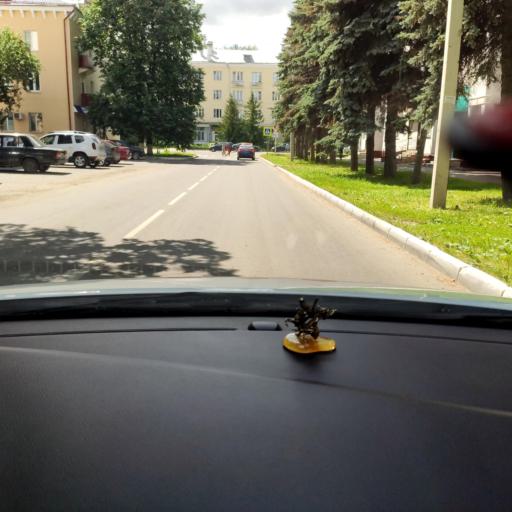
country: RU
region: Tatarstan
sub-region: Zelenodol'skiy Rayon
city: Zelenodolsk
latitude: 55.8475
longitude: 48.4980
